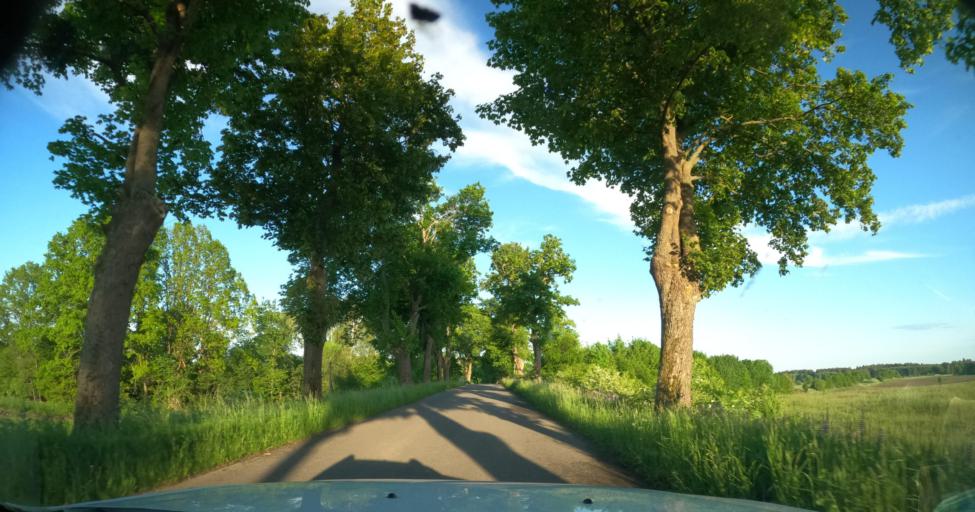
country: PL
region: Warmian-Masurian Voivodeship
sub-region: Powiat lidzbarski
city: Orneta
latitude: 54.1754
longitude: 20.1435
